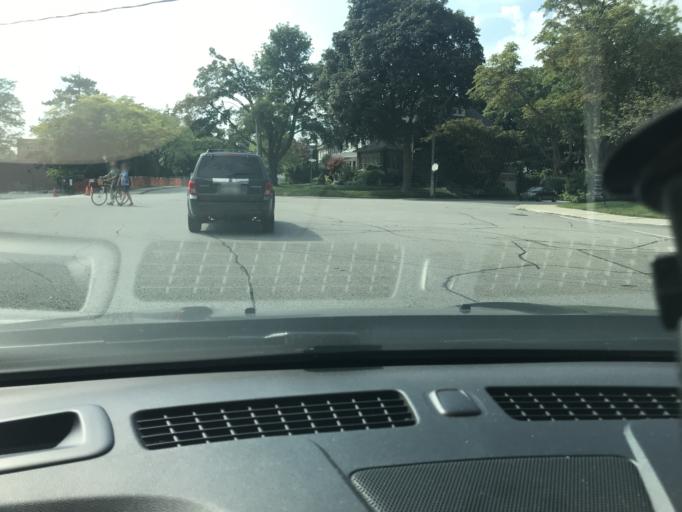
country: CA
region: Ontario
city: Toronto
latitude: 43.7218
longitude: -79.4077
